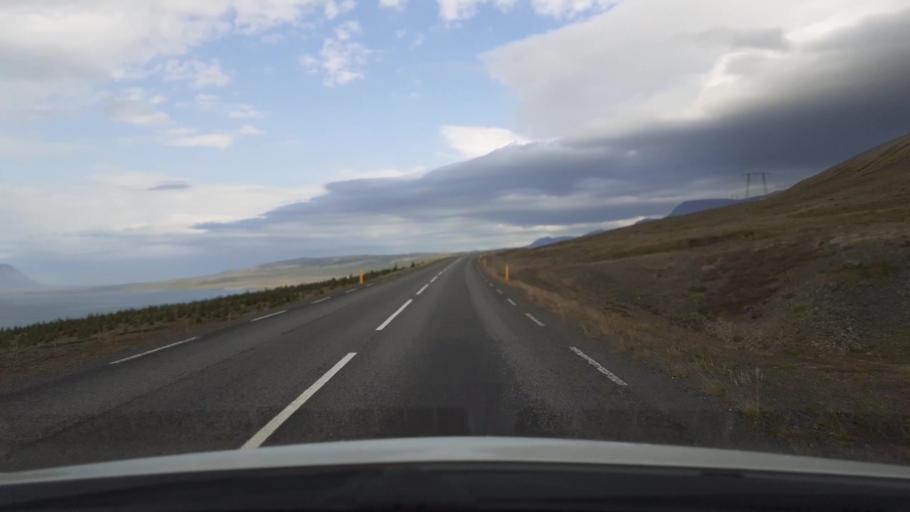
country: IS
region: Capital Region
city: Mosfellsbaer
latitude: 64.4025
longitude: -21.5578
